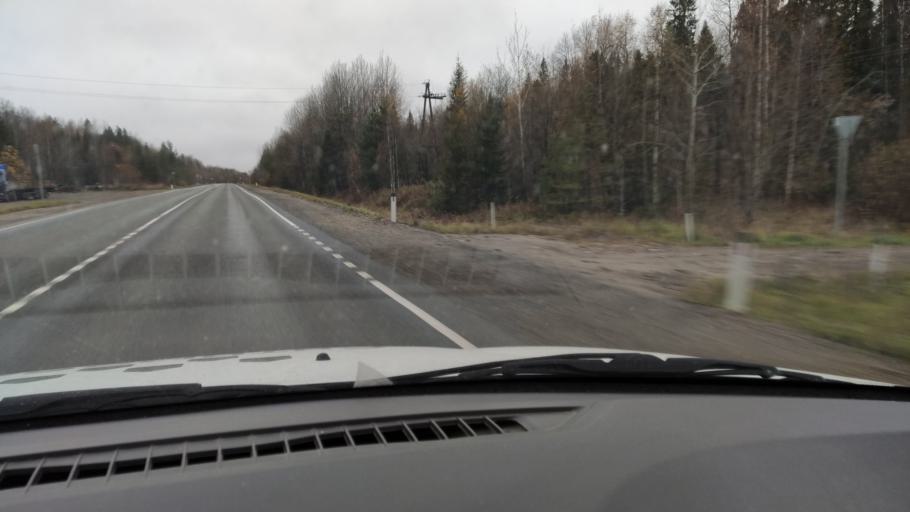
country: RU
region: Kirov
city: Omutninsk
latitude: 58.6994
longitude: 52.1181
